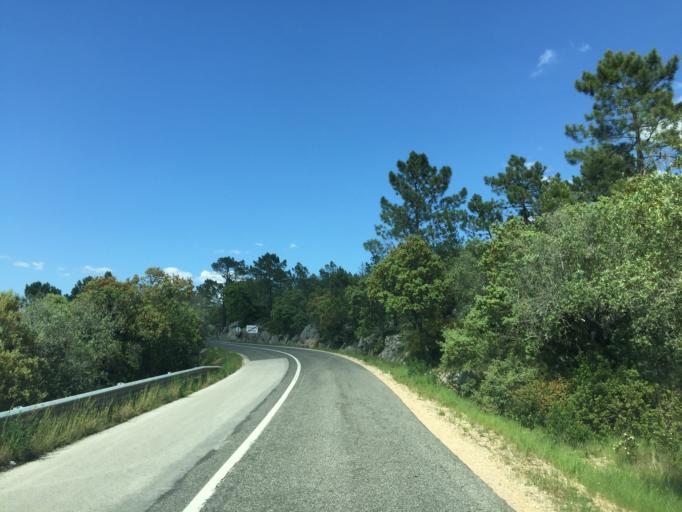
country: PT
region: Leiria
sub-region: Alvaiazere
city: Alvaiazere
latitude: 39.7869
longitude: -8.4328
